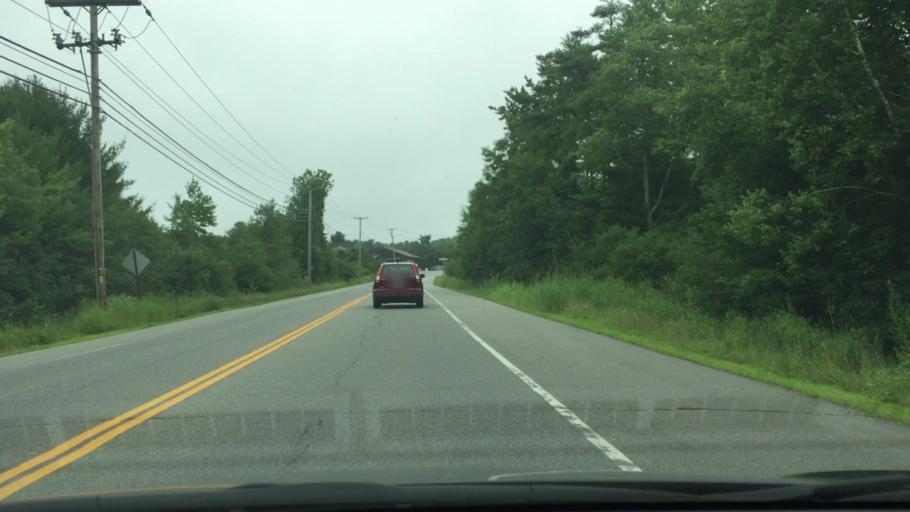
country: US
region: Maine
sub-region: York County
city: Cape Neddick
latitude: 43.2035
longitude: -70.6200
